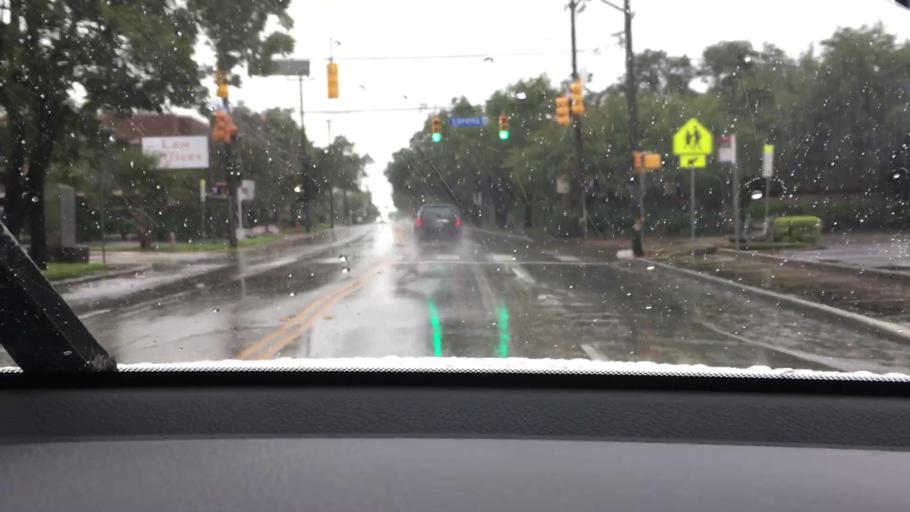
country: US
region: Texas
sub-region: Bexar County
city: Alamo Heights
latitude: 29.5027
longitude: -98.4666
